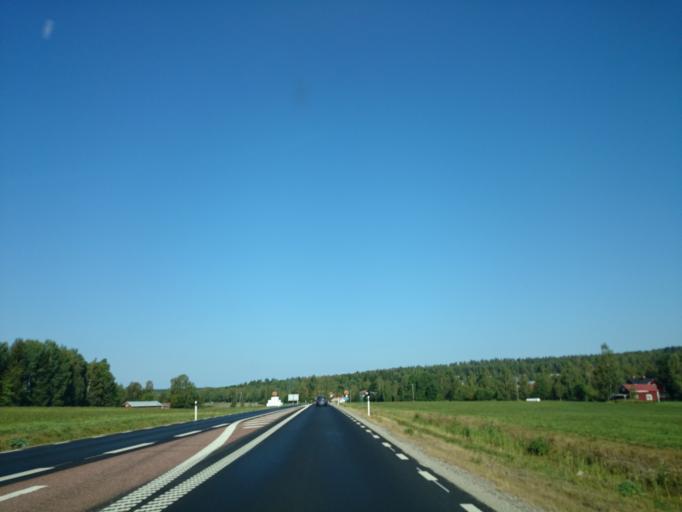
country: SE
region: Gaevleborg
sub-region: Hudiksvalls Kommun
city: Sorforsa
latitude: 61.7299
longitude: 16.9630
